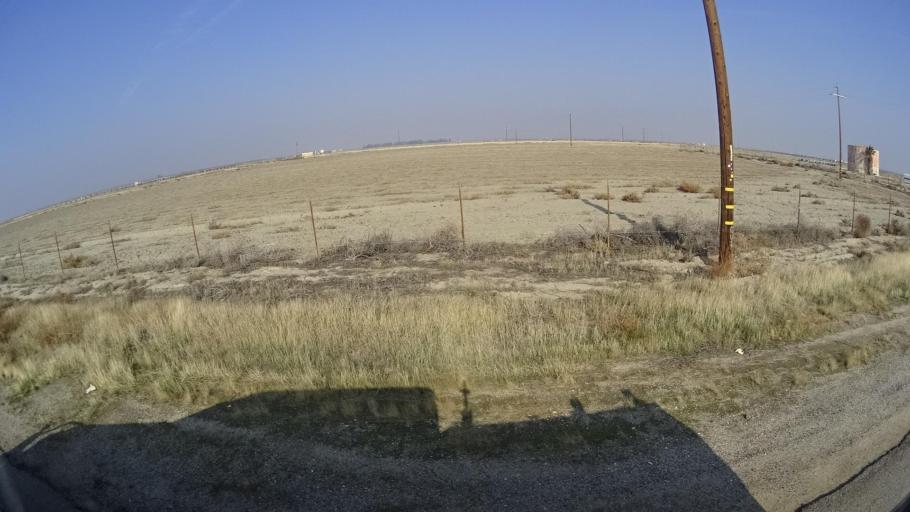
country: US
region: California
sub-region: Kern County
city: Buttonwillow
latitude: 35.3331
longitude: -119.3655
